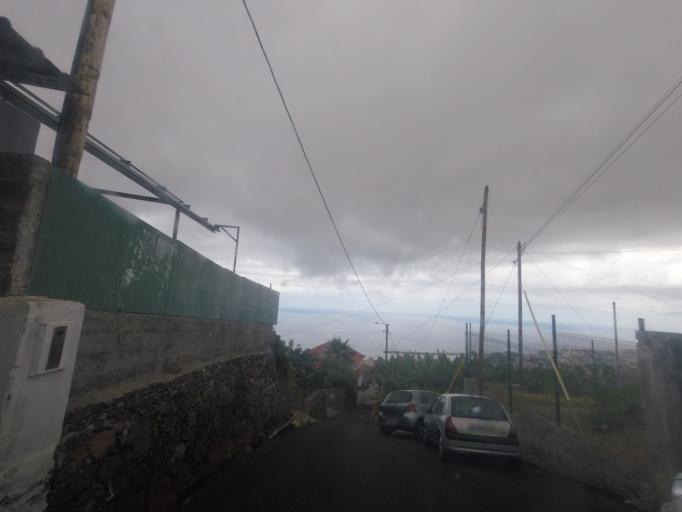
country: PT
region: Madeira
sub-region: Funchal
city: Nossa Senhora do Monte
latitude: 32.6664
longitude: -16.9001
